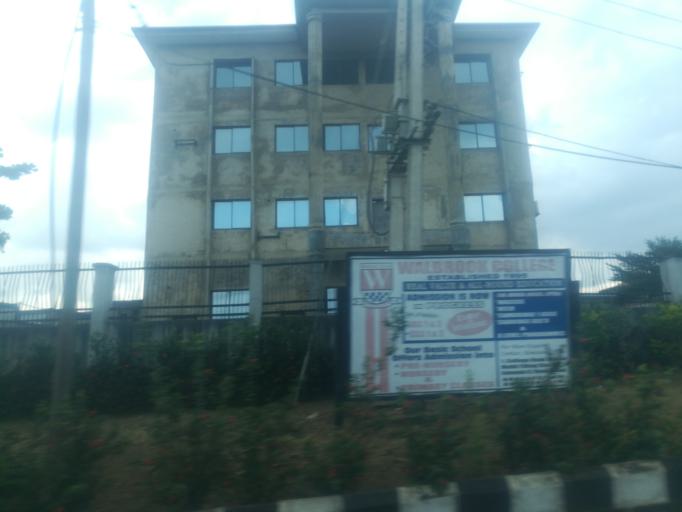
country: NG
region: Oyo
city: Ibadan
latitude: 7.4337
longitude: 3.9060
